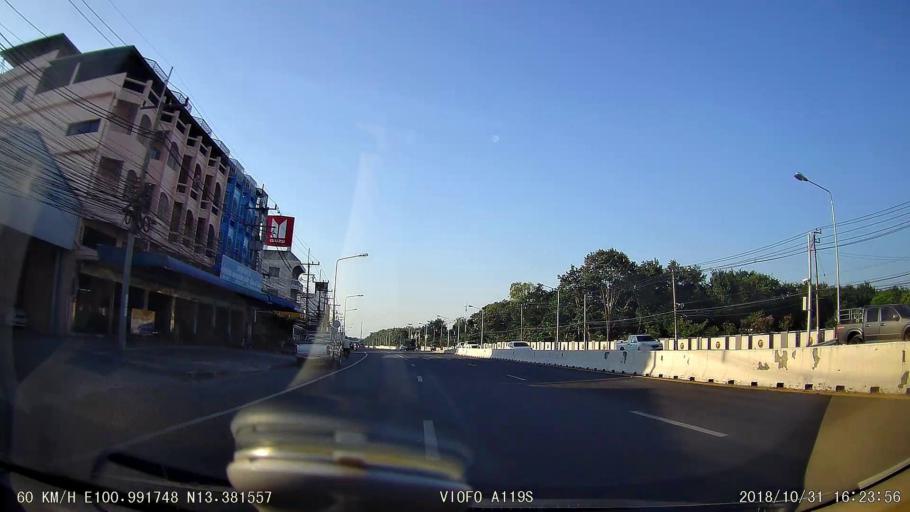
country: TH
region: Chon Buri
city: Chon Buri
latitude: 13.3819
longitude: 100.9916
